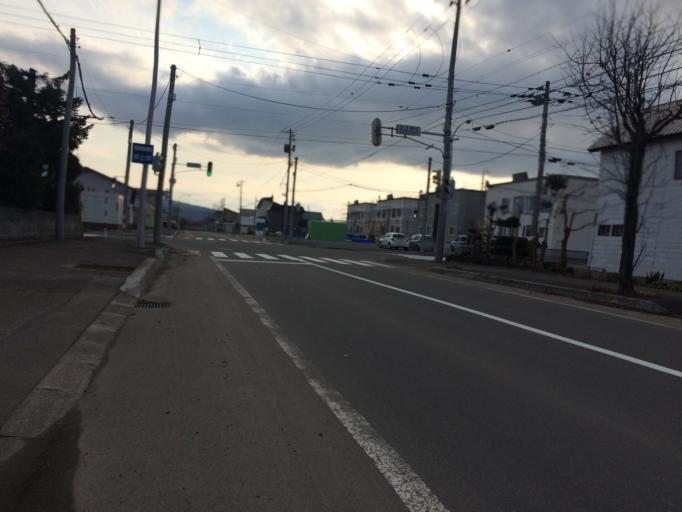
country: JP
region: Hokkaido
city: Niseko Town
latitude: 42.9011
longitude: 140.7663
